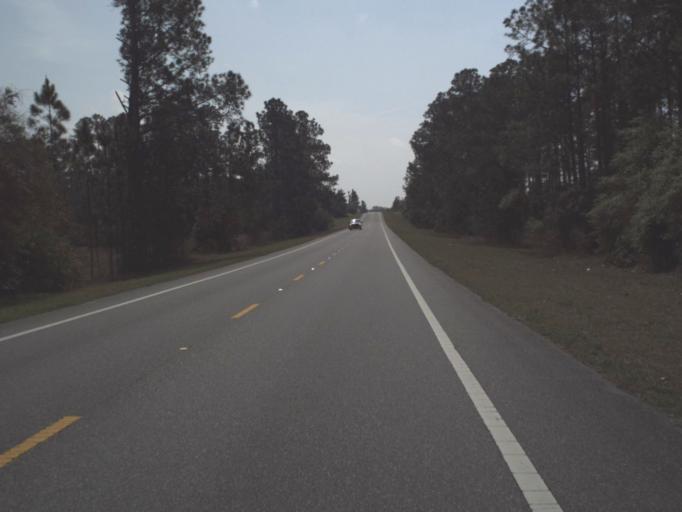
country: US
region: Florida
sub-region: Lake County
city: Astor
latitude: 29.1426
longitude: -81.6293
